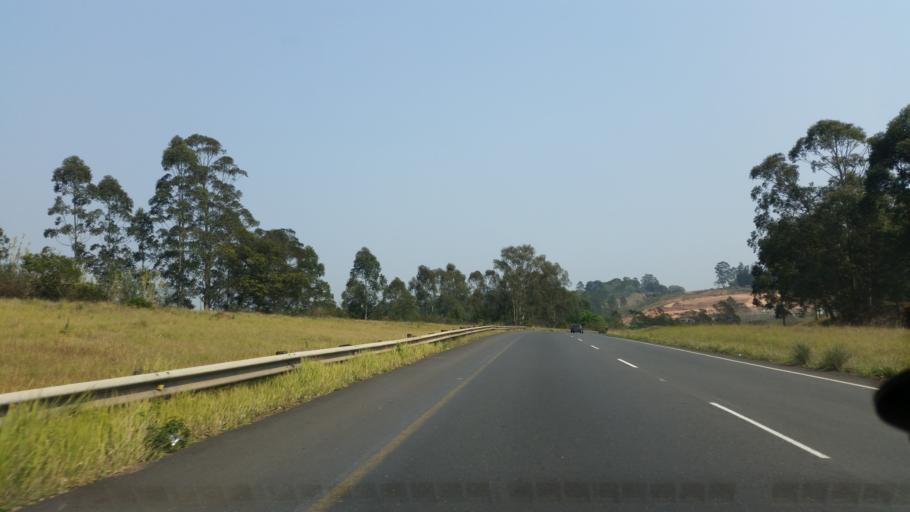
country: ZA
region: KwaZulu-Natal
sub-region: eThekwini Metropolitan Municipality
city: Mpumalanga
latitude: -29.7938
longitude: 30.7413
